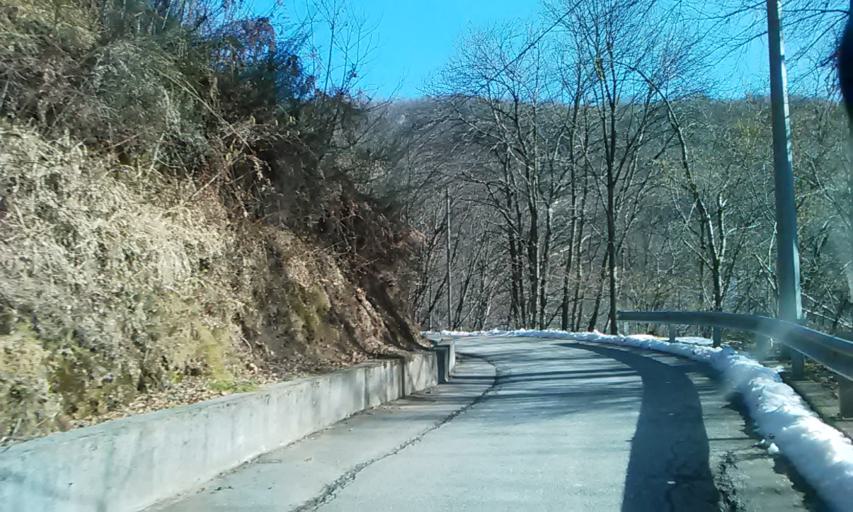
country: IT
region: Piedmont
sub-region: Provincia di Vercelli
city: Breia
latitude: 45.7710
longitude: 8.3257
